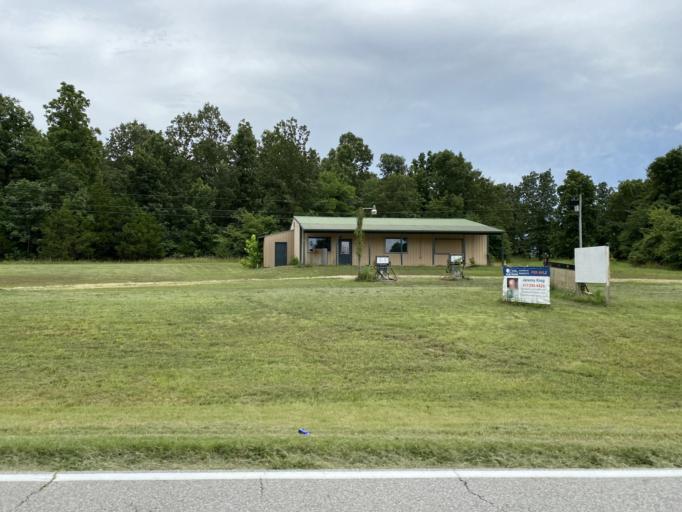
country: US
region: Arkansas
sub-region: Fulton County
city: Salem
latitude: 36.4173
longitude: -91.7232
